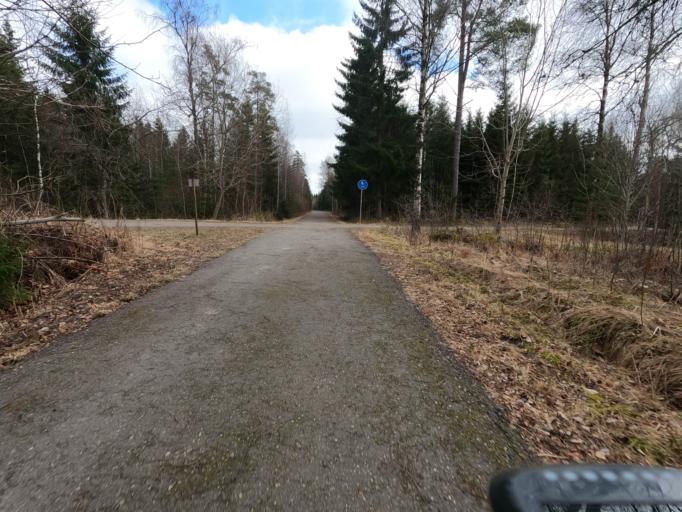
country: SE
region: Joenkoeping
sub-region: Varnamo Kommun
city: Rydaholm
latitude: 56.8537
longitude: 14.1888
